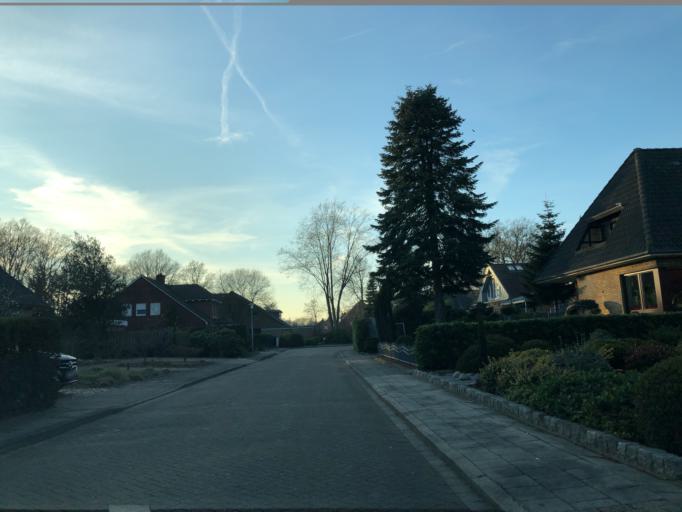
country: DE
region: Lower Saxony
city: Papenburg
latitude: 53.0680
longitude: 7.4003
